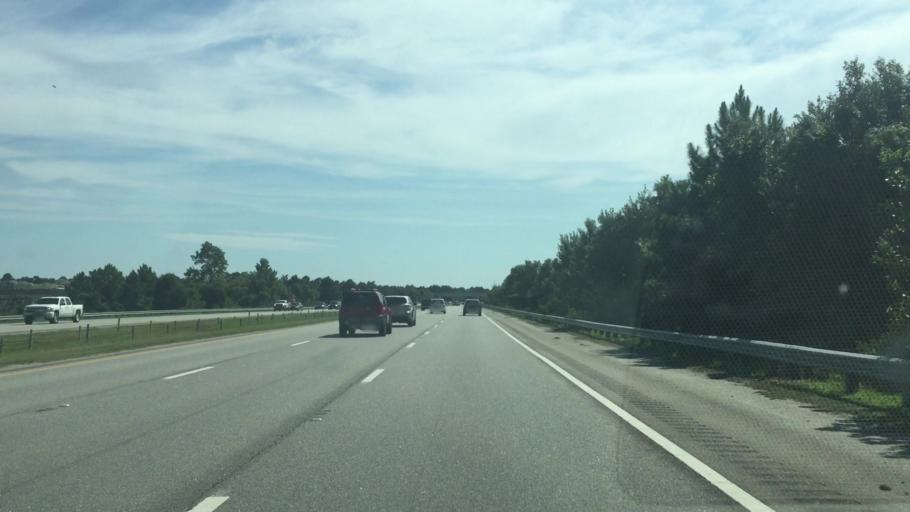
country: US
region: South Carolina
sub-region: Horry County
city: North Myrtle Beach
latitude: 33.8227
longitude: -78.7361
